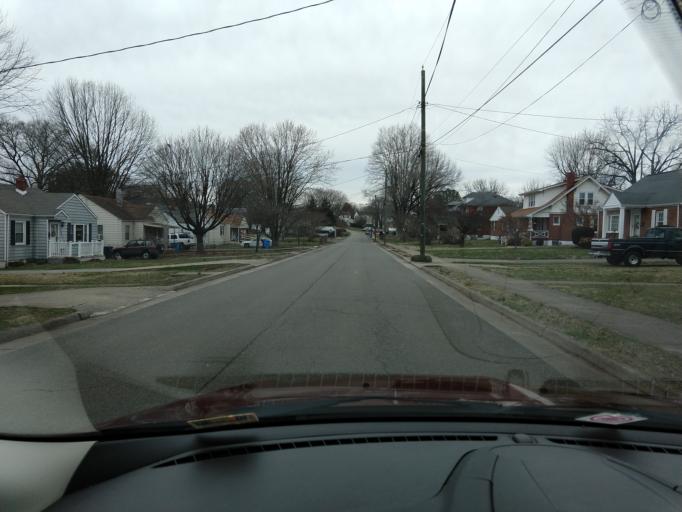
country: US
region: Virginia
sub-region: City of Roanoke
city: Roanoke
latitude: 37.3034
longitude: -79.9373
